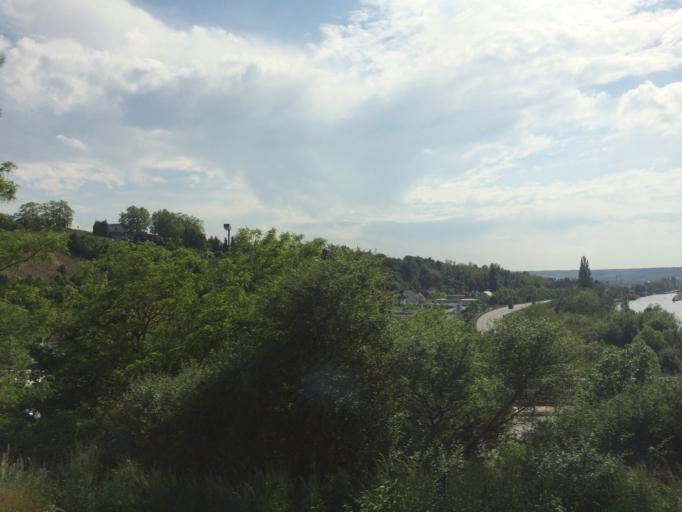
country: DE
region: Bavaria
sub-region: Regierungsbezirk Unterfranken
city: Kitzingen
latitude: 49.7254
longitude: 10.1659
